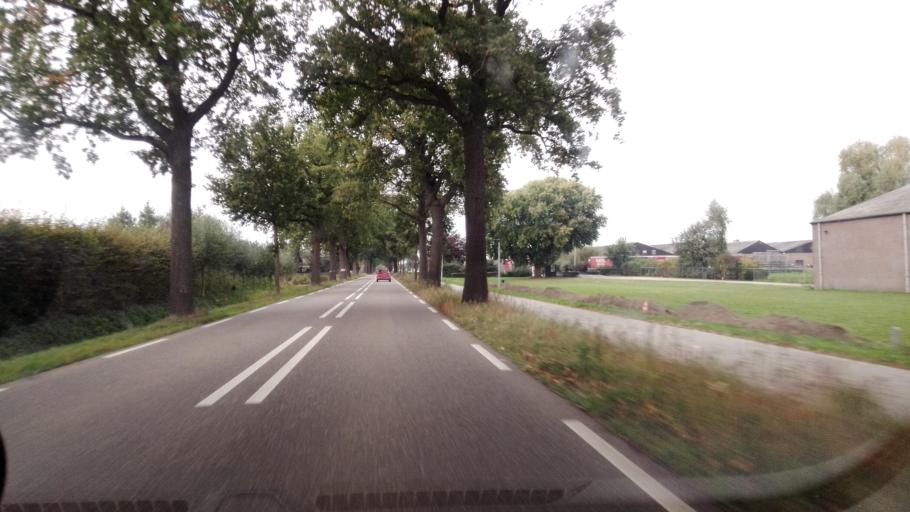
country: NL
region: Limburg
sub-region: Gemeente Peel en Maas
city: Maasbree
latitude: 51.4288
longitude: 6.0968
